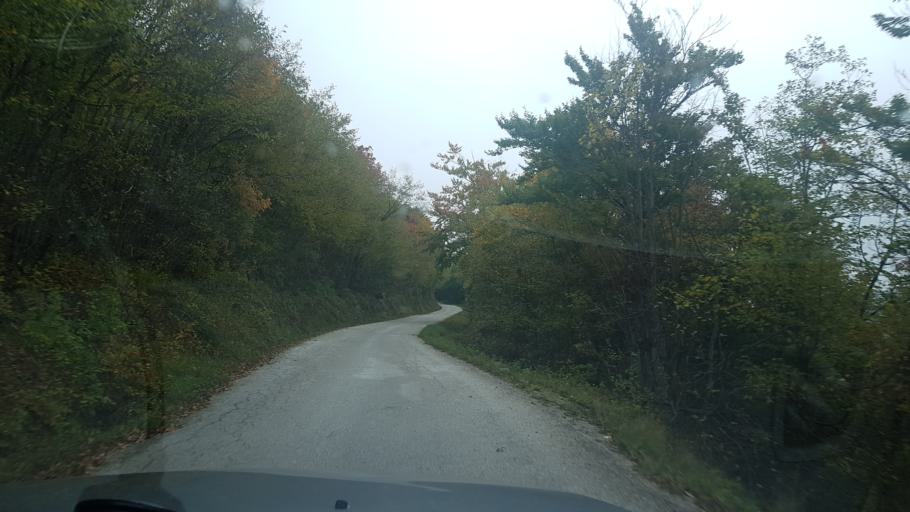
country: HR
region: Istarska
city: Buzet
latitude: 45.4589
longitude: 14.0347
